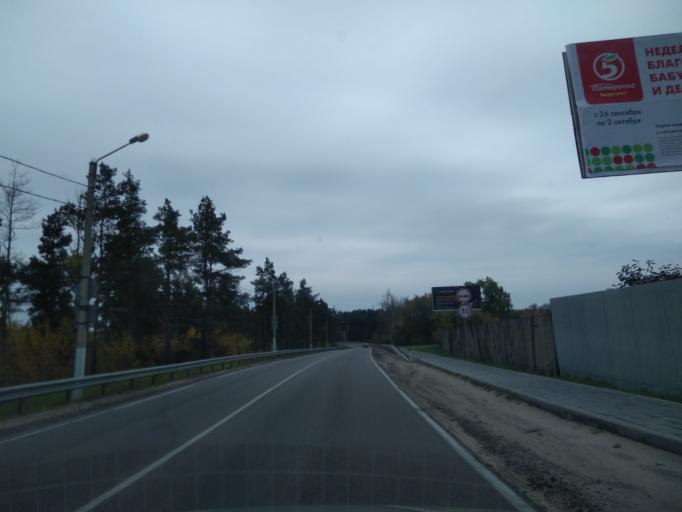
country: RU
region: Lipetsk
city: Zadonsk
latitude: 52.3835
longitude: 38.9373
